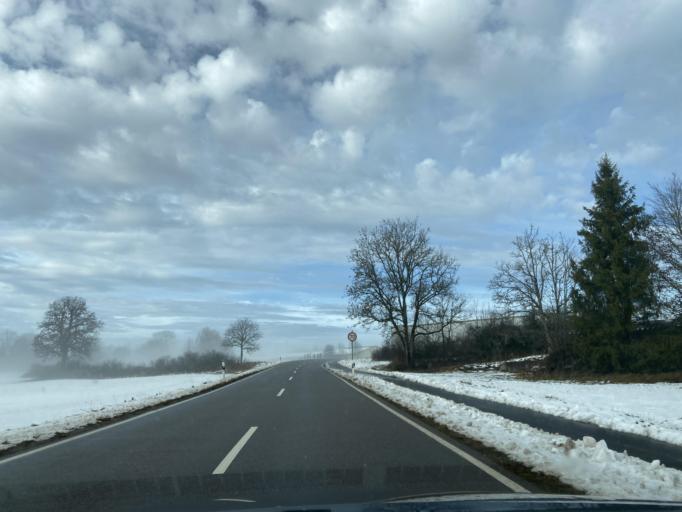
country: DE
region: Baden-Wuerttemberg
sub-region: Tuebingen Region
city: Hettingen
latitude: 48.2096
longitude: 9.2490
